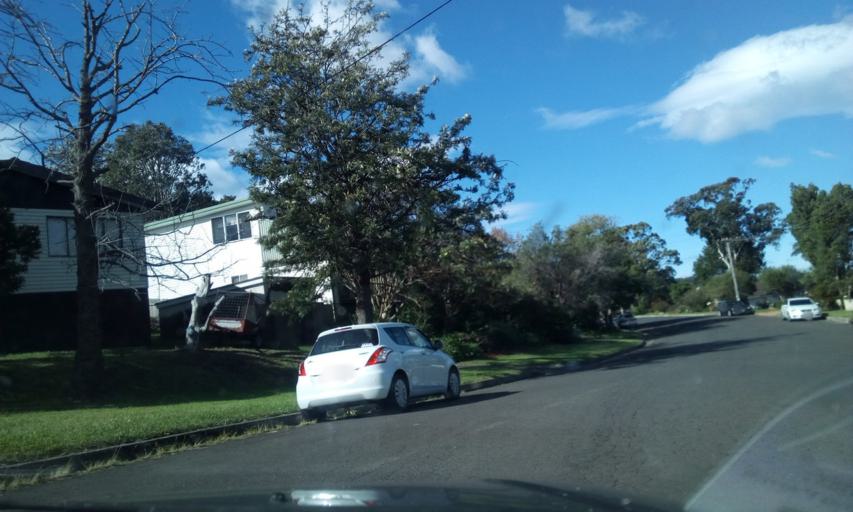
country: AU
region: New South Wales
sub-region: Wollongong
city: West Wollongong
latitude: -34.4229
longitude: 150.8649
